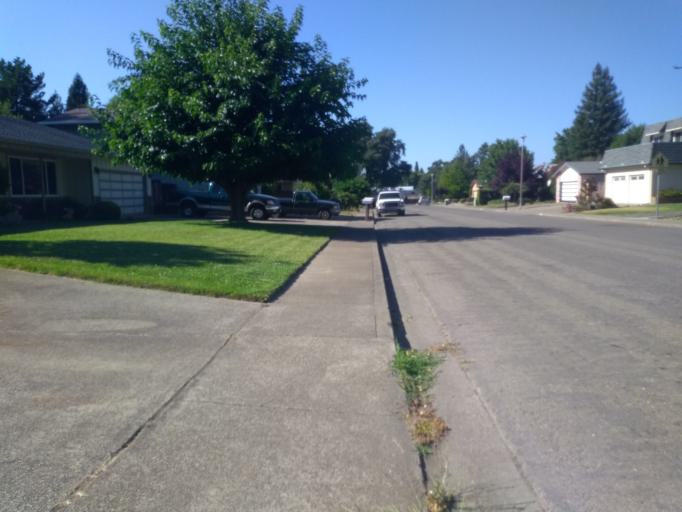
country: US
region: California
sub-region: Mendocino County
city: Ukiah
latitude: 39.1304
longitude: -123.2116
